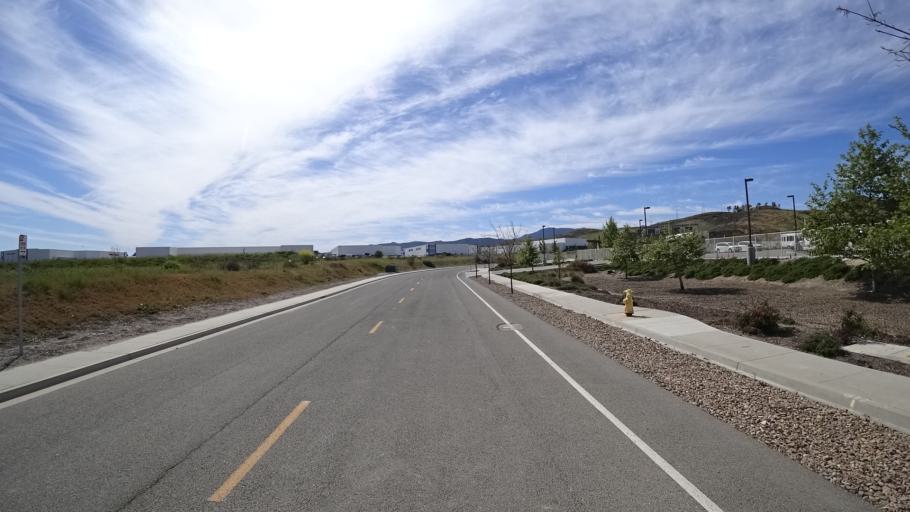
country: US
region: California
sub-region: Ventura County
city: Casa Conejo
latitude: 34.2048
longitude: -118.9332
